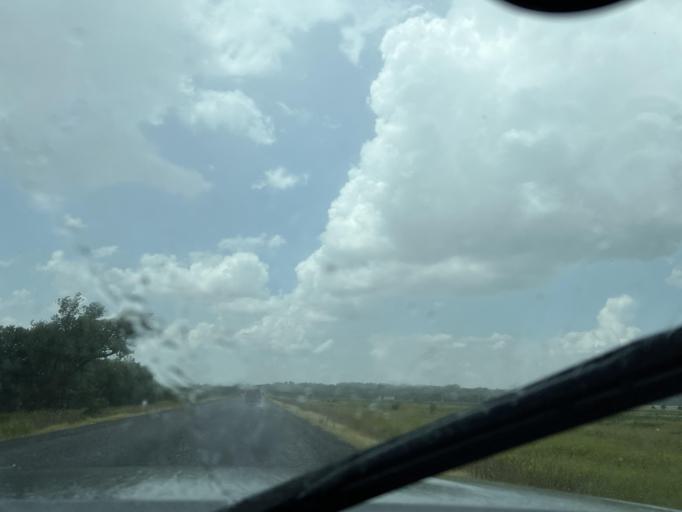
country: US
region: Texas
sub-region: Wise County
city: Boyd
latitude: 33.1277
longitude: -97.6488
